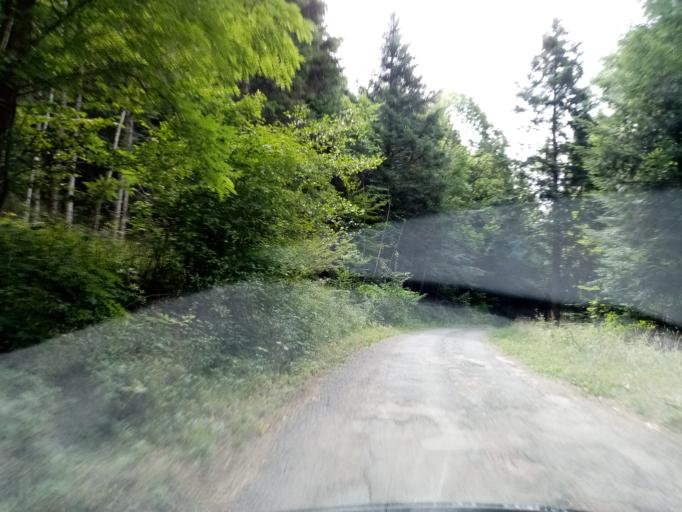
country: FR
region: Alsace
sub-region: Departement du Bas-Rhin
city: Ville
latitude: 48.3573
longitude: 7.3466
